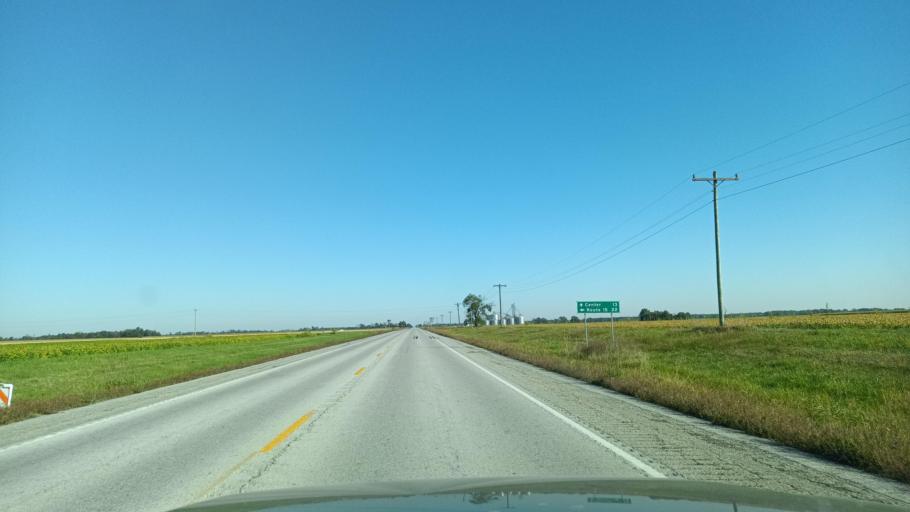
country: US
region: Missouri
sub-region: Audrain County
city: Vandalia
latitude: 39.3581
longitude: -91.6425
